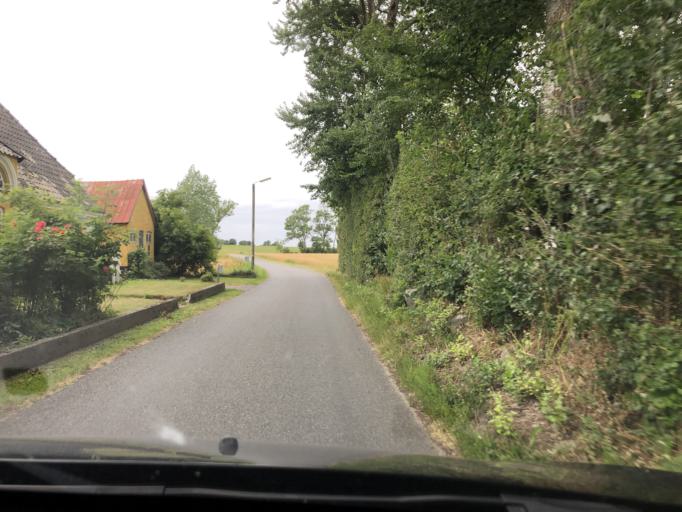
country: DK
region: South Denmark
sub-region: AEro Kommune
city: AEroskobing
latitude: 54.9153
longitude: 10.2940
